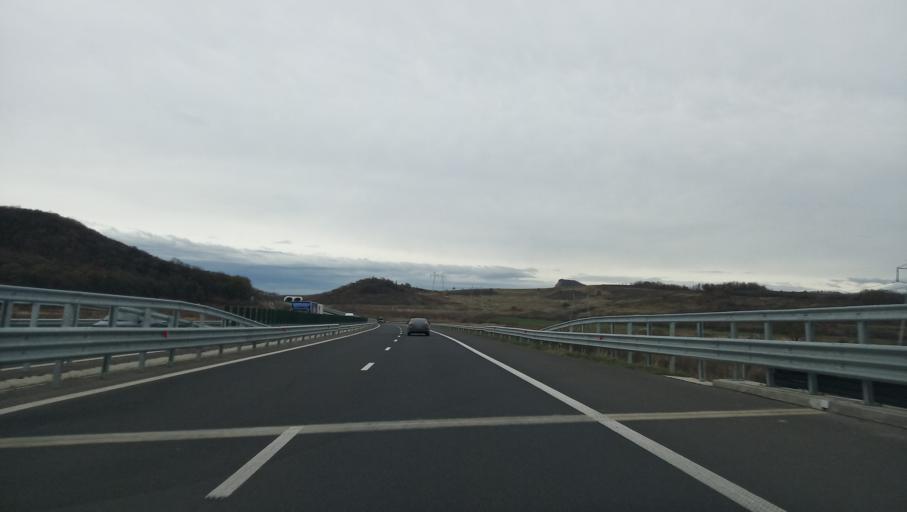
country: RO
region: Hunedoara
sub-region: Comuna Branisca
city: Branisca
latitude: 45.9356
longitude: 22.7545
